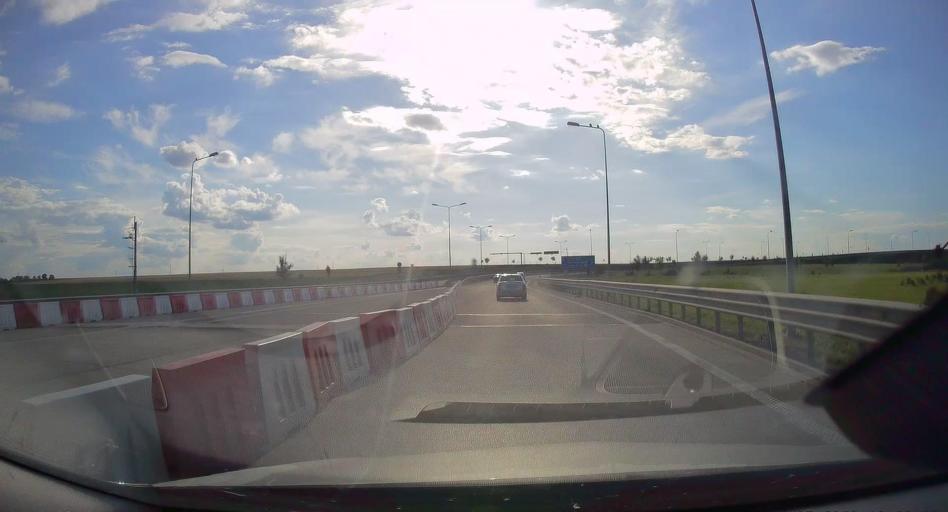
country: PL
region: Subcarpathian Voivodeship
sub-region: Powiat przemyski
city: Orly
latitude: 49.9085
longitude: 22.8135
